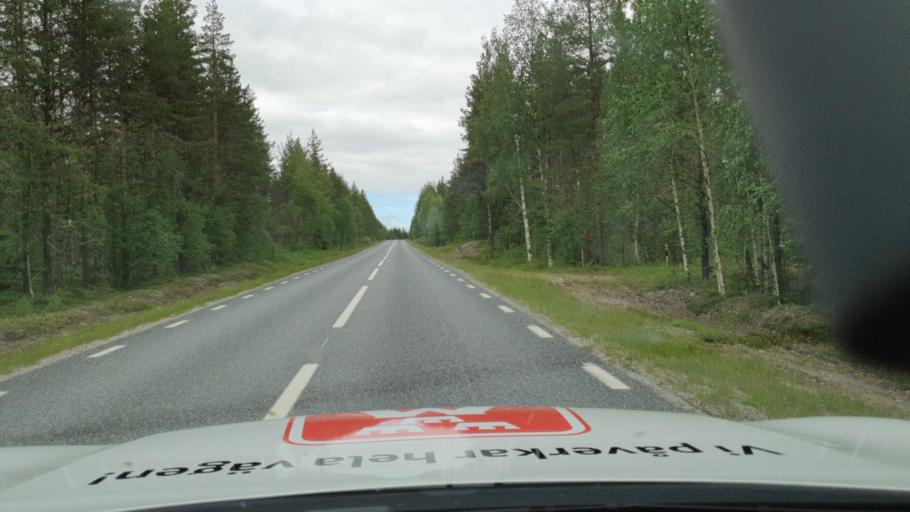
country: SE
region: Vaesterbotten
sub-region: Asele Kommun
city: Insjon
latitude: 64.2375
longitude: 17.5499
